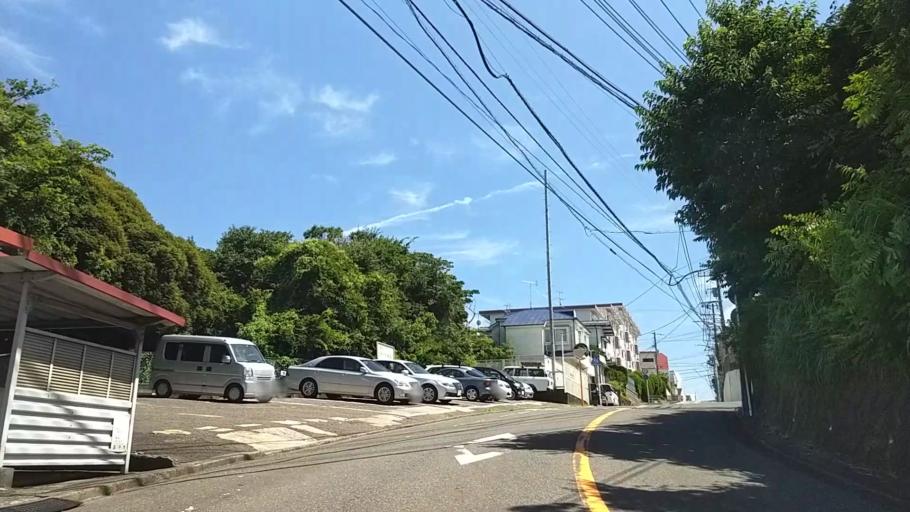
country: JP
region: Kanagawa
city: Zushi
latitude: 35.2923
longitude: 139.5910
